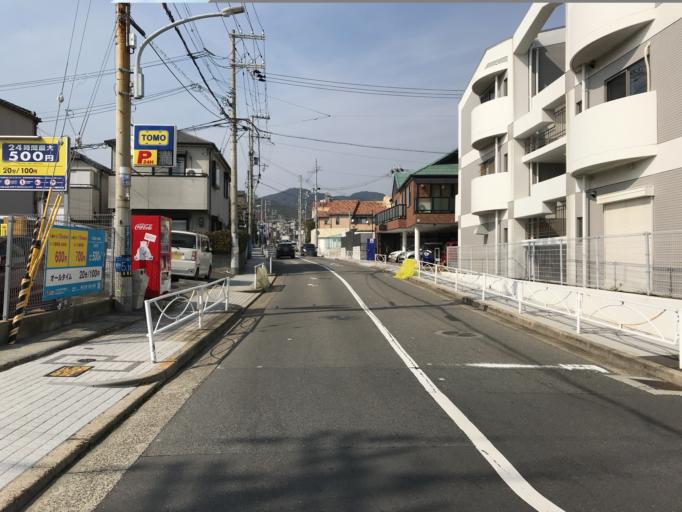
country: JP
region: Hyogo
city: Kobe
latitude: 34.6446
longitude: 135.1216
